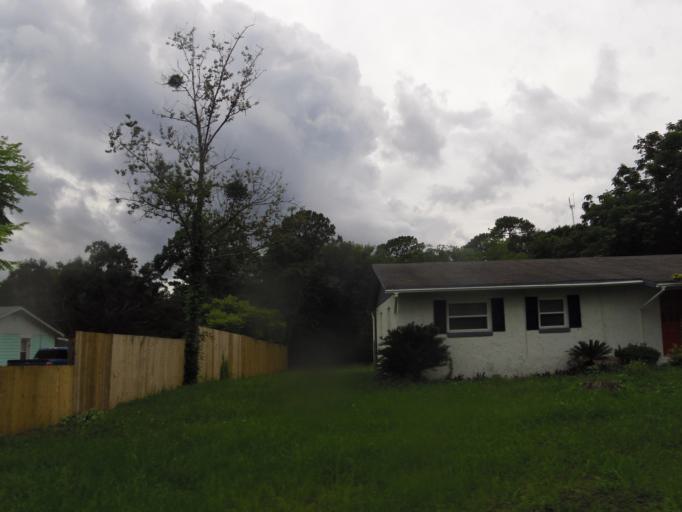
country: US
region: Florida
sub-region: Duval County
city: Jacksonville
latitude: 30.2691
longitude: -81.5430
